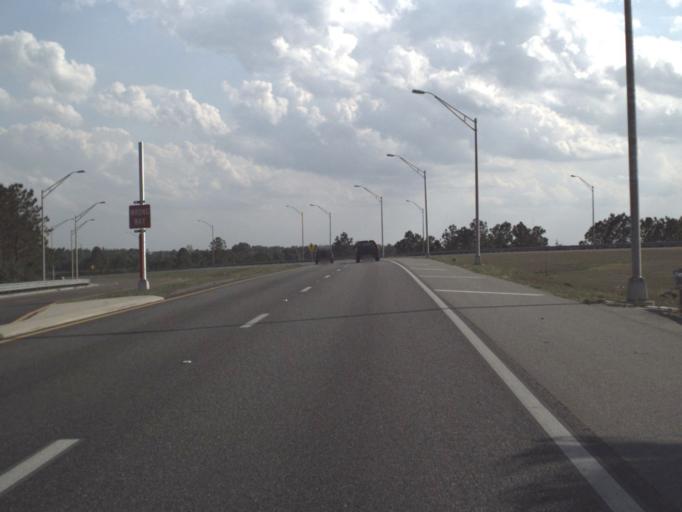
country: US
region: Florida
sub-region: Orange County
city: Apopka
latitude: 28.6809
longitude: -81.5281
